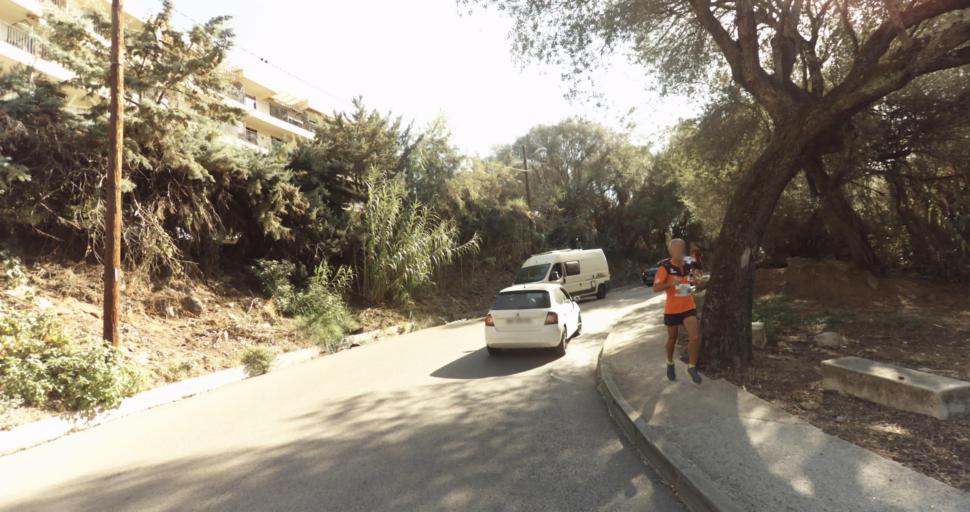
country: FR
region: Corsica
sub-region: Departement de la Corse-du-Sud
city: Ajaccio
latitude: 41.9203
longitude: 8.7271
